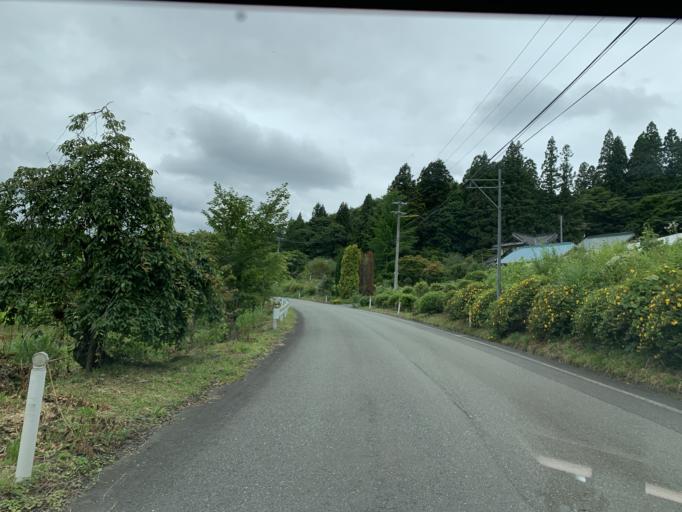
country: JP
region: Iwate
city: Ichinoseki
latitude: 38.9021
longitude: 140.9897
